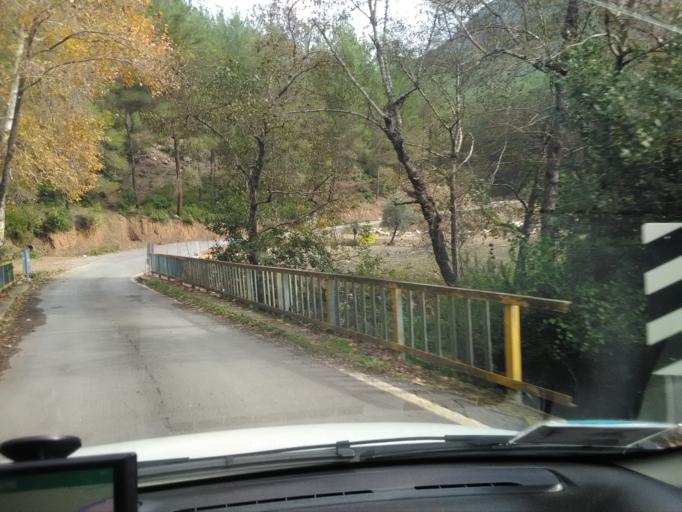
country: TR
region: Antalya
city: Gazipasa
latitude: 36.2454
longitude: 32.4123
